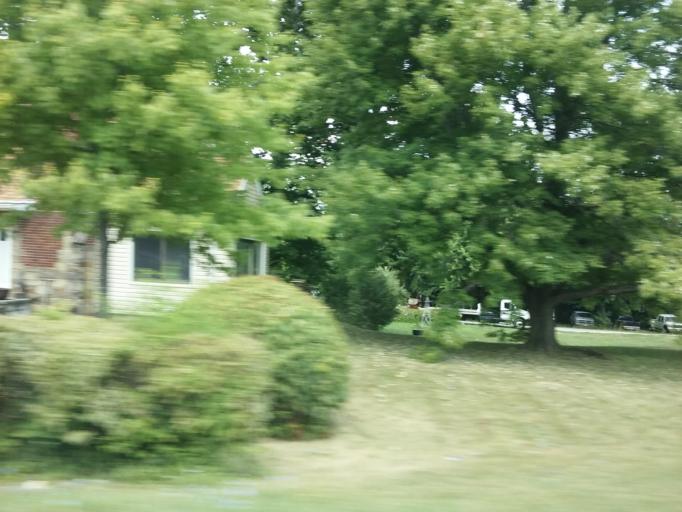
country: US
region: Ohio
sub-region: Hancock County
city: Findlay
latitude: 41.0424
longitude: -83.6797
